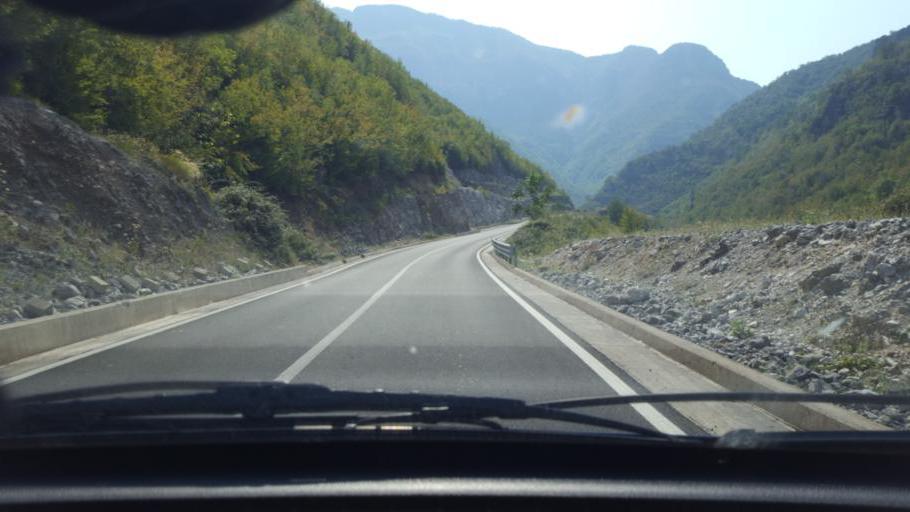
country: AL
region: Shkoder
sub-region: Rrethi i Malesia e Madhe
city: Kastrat
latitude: 42.4374
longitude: 19.5385
